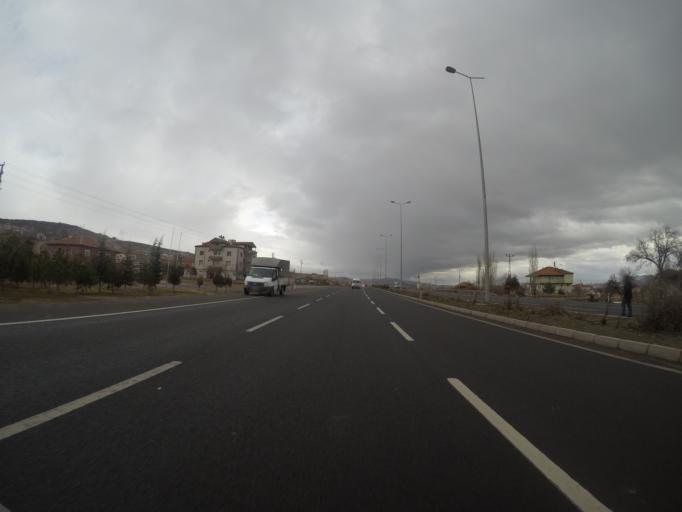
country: TR
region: Kayseri
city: Incesu
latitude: 38.7341
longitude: 35.2869
